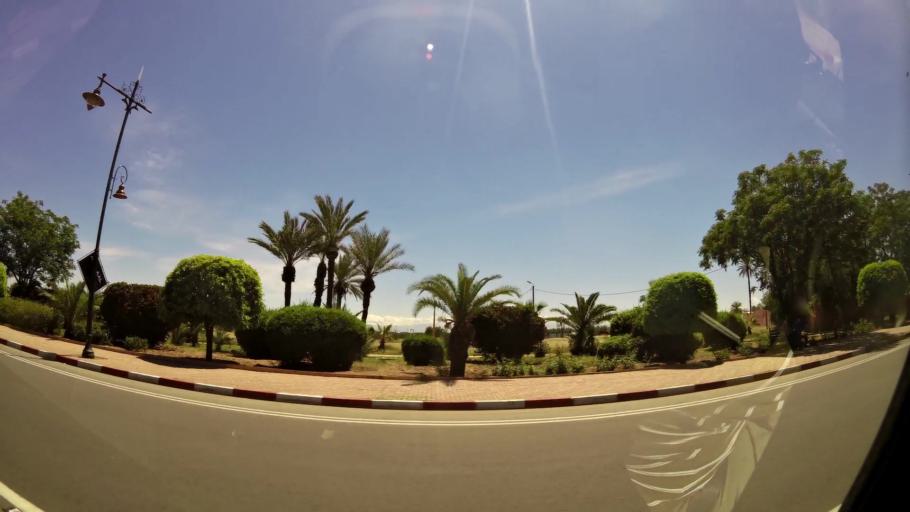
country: MA
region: Marrakech-Tensift-Al Haouz
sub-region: Marrakech
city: Marrakesh
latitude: 31.6199
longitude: -8.0031
